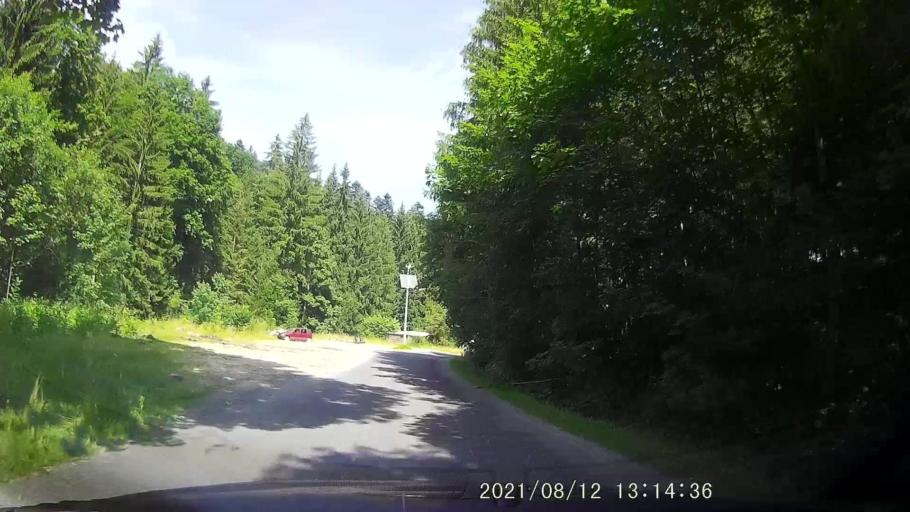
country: PL
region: Lower Silesian Voivodeship
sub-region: Powiat klodzki
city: Stronie Slaskie
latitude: 50.2593
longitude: 16.8610
